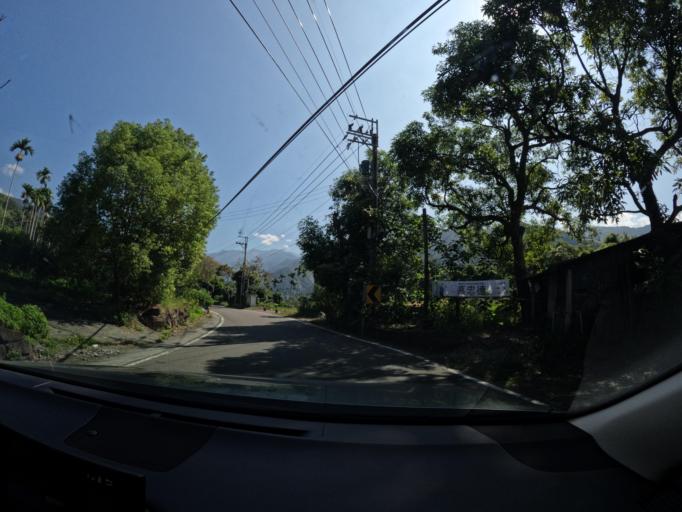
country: TW
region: Taiwan
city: Yujing
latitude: 23.1256
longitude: 120.7131
